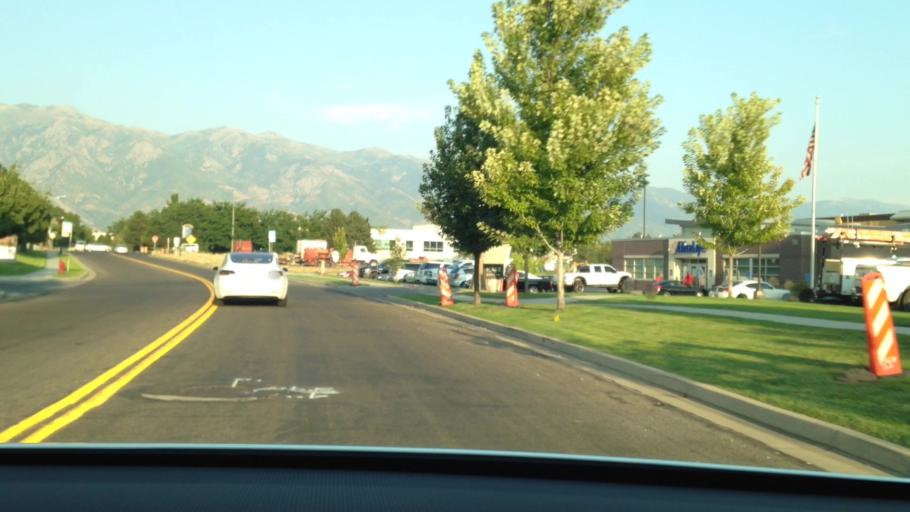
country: US
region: Utah
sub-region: Davis County
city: Layton
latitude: 41.0832
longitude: -111.9805
